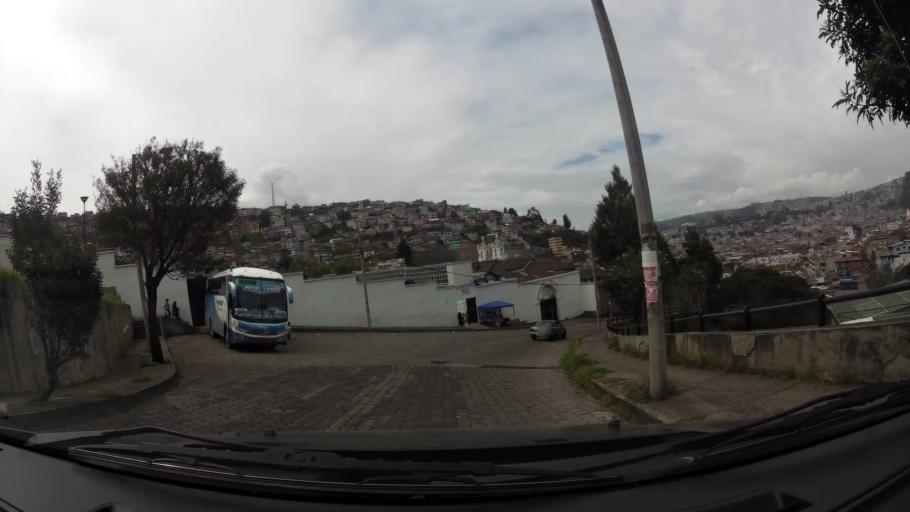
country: EC
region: Pichincha
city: Quito
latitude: -0.2145
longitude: -78.5188
